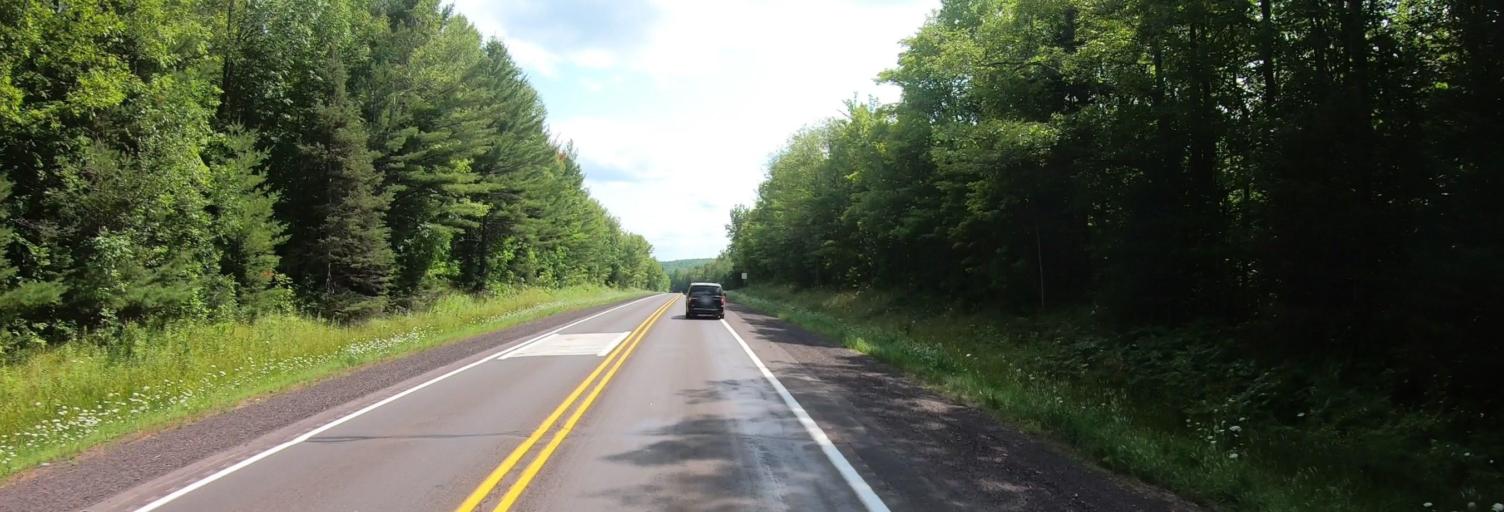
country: US
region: Michigan
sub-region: Ontonagon County
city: Ontonagon
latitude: 46.7730
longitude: -89.0736
